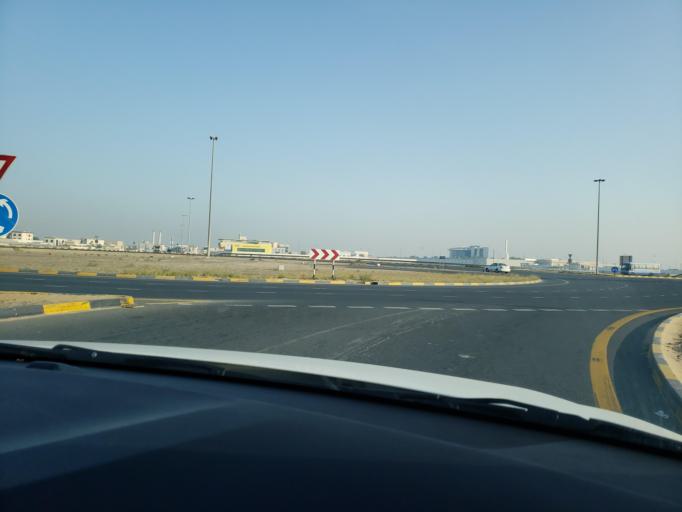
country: AE
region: Umm al Qaywayn
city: Umm al Qaywayn
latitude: 25.5073
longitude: 55.5946
